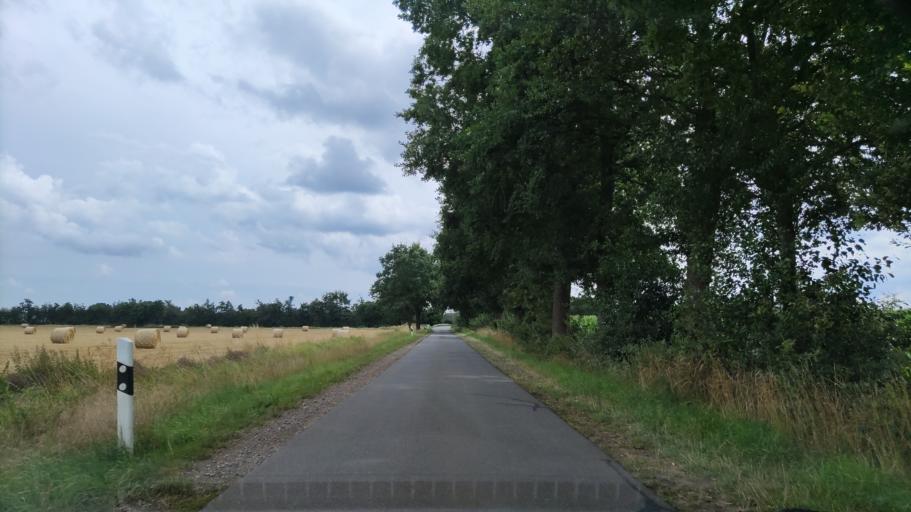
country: DE
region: Lower Saxony
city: Klein Gusborn
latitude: 53.0875
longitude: 11.1422
